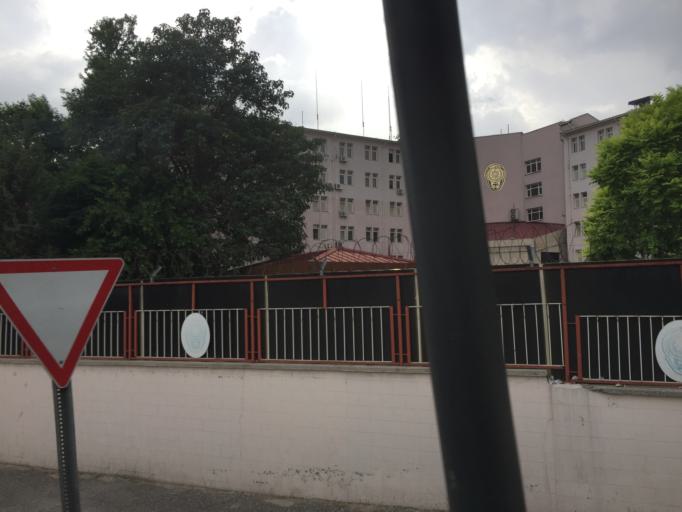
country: TR
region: Gaziantep
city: Gaziantep
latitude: 37.0665
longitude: 37.3753
